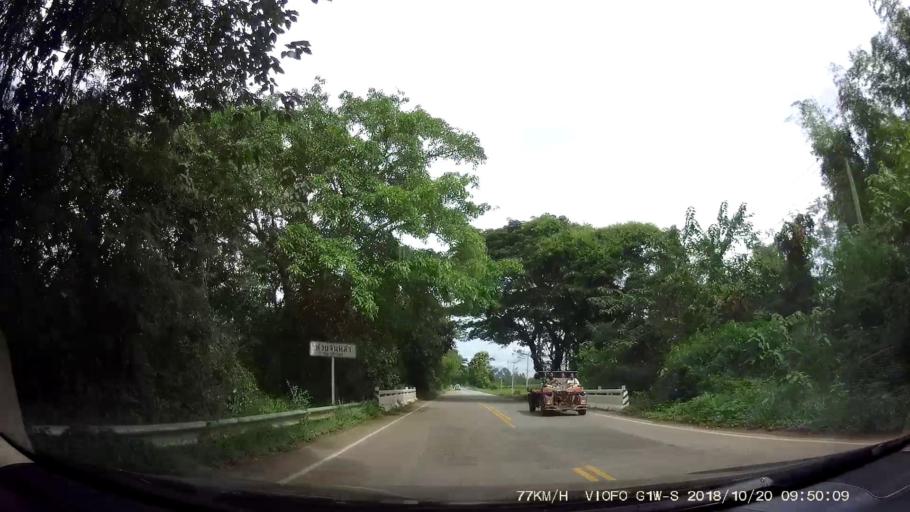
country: TH
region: Chaiyaphum
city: Khon San
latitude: 16.5280
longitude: 101.9030
